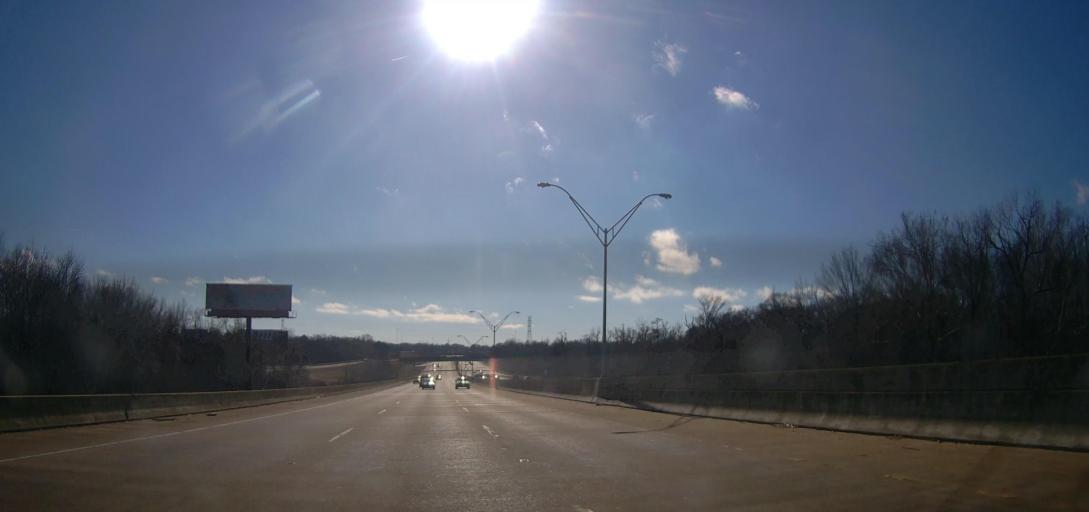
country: US
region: Tennessee
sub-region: Shelby County
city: Bartlett
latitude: 35.2020
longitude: -89.9241
